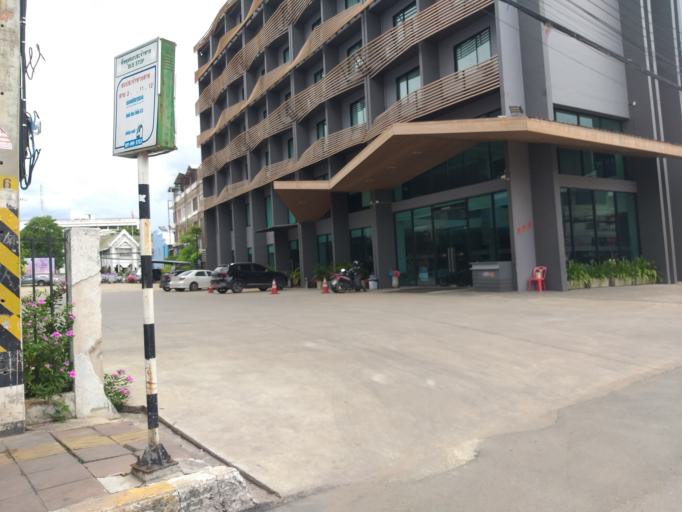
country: TH
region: Nakhon Ratchasima
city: Nakhon Ratchasima
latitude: 14.9752
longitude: 102.0858
